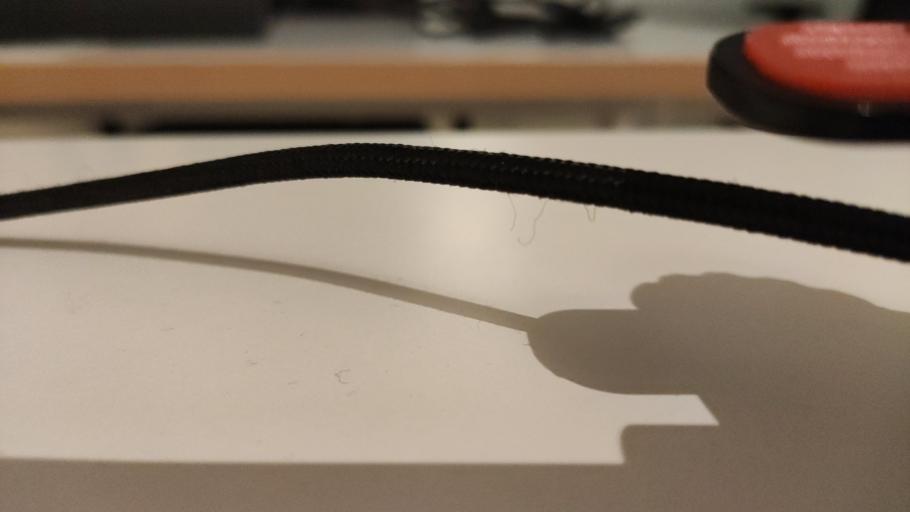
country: RU
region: Moskovskaya
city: Novoye
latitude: 55.6284
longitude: 38.9437
